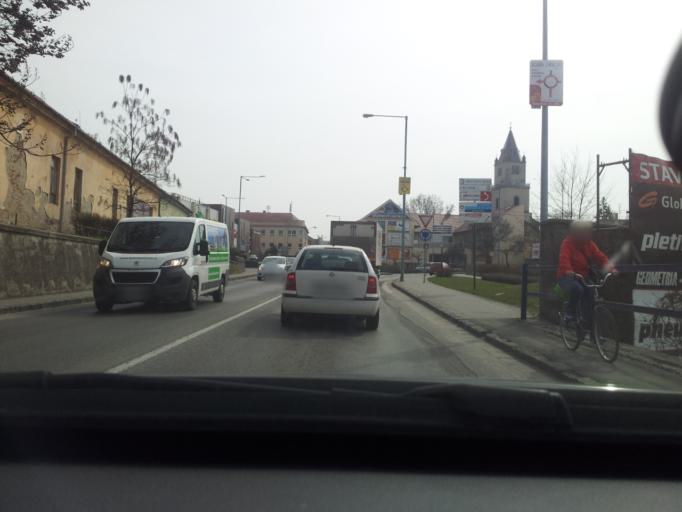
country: SK
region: Trnavsky
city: Hlohovec
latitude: 48.4284
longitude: 17.7952
